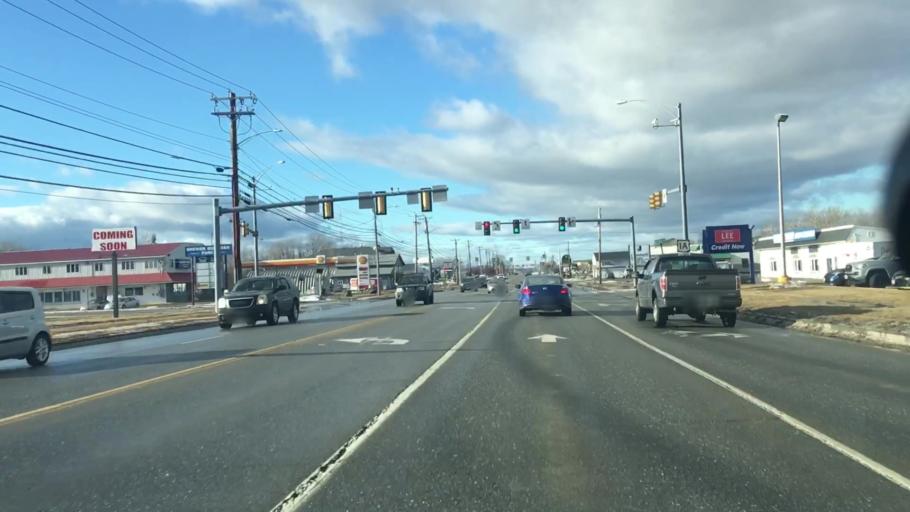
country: US
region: Maine
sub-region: Penobscot County
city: Brewer
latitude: 44.7777
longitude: -68.7363
